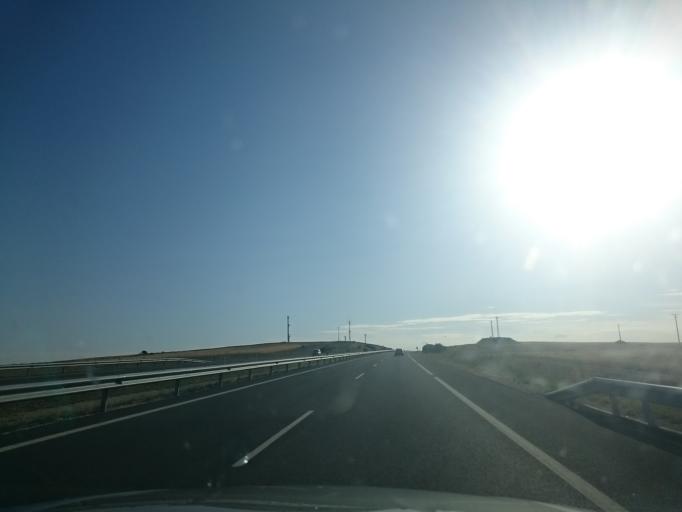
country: ES
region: Castille and Leon
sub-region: Provincia de Burgos
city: Rabe de las Calzadas
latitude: 42.3694
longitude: -3.8755
